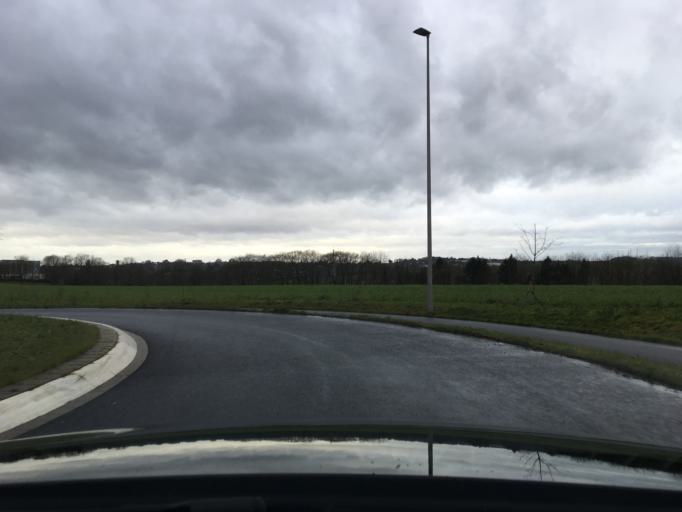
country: DE
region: North Rhine-Westphalia
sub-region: Regierungsbezirk Dusseldorf
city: Mettmann
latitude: 51.2607
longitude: 6.9949
